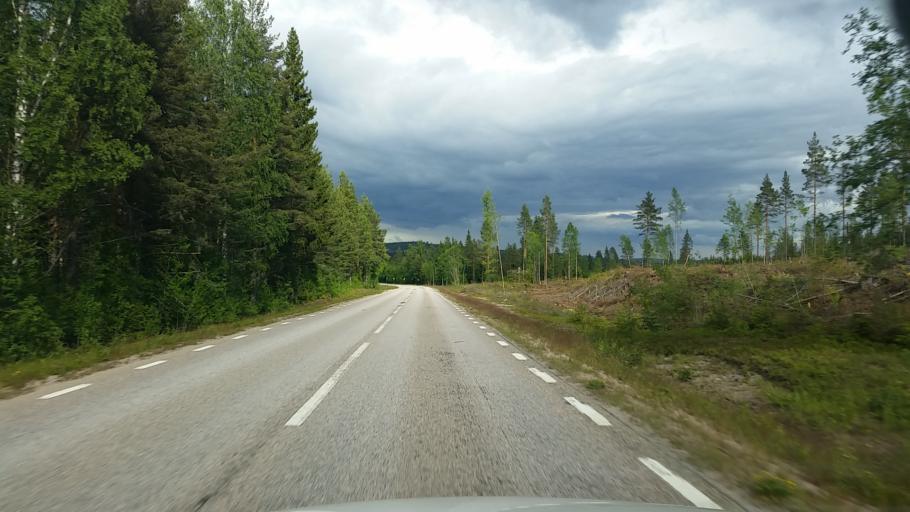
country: SE
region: Jaemtland
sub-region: Harjedalens Kommun
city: Sveg
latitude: 61.9791
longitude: 15.1119
